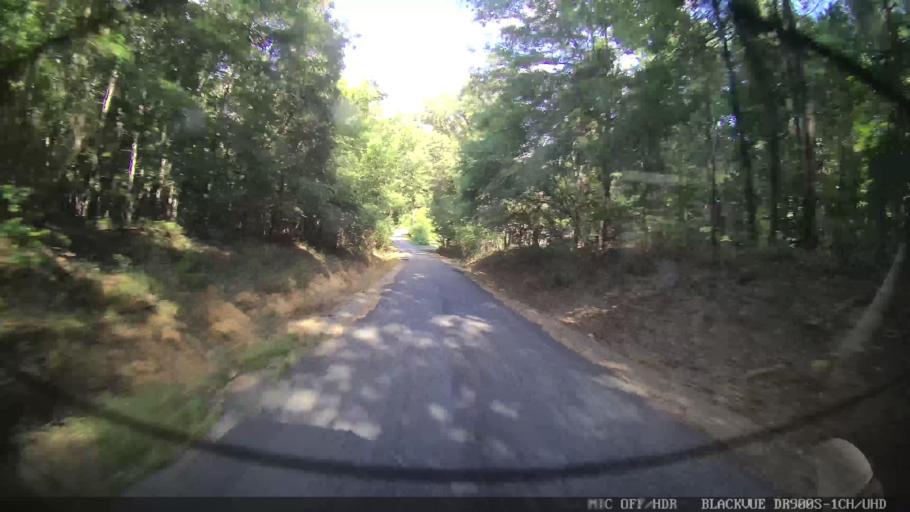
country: US
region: Georgia
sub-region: Floyd County
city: Lindale
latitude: 34.2150
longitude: -85.1283
